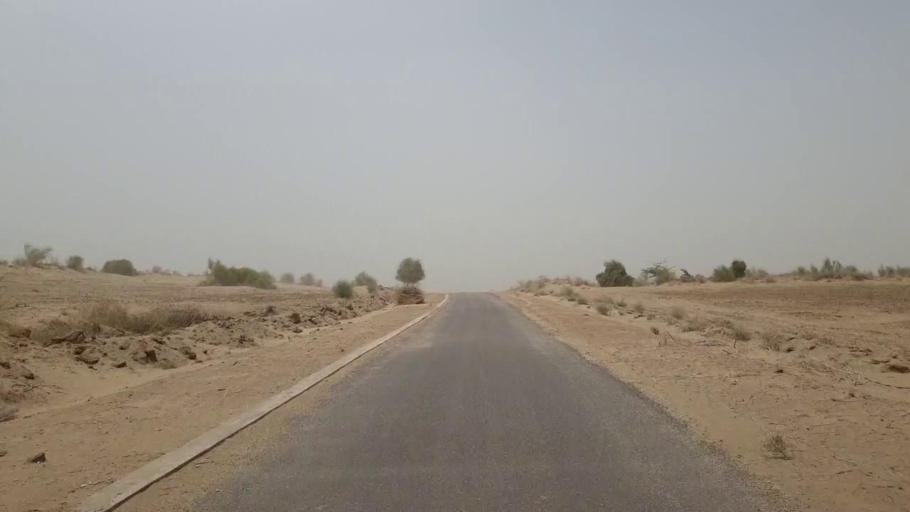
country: PK
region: Sindh
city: Islamkot
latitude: 24.8051
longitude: 70.5258
